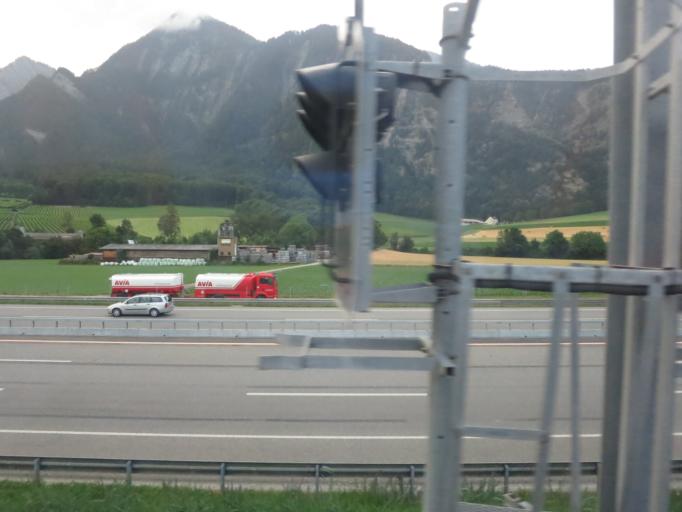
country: CH
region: Grisons
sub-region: Landquart District
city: Trimmis
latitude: 46.9161
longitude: 9.5609
